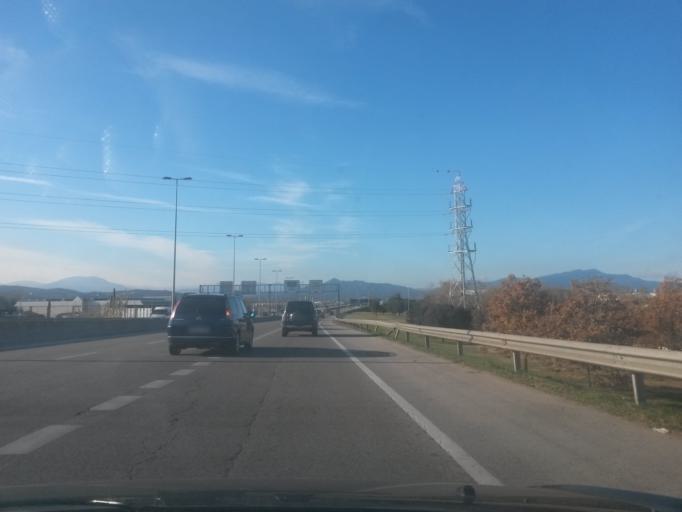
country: ES
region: Catalonia
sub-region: Provincia de Girona
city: Salt
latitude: 41.9576
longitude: 2.8075
